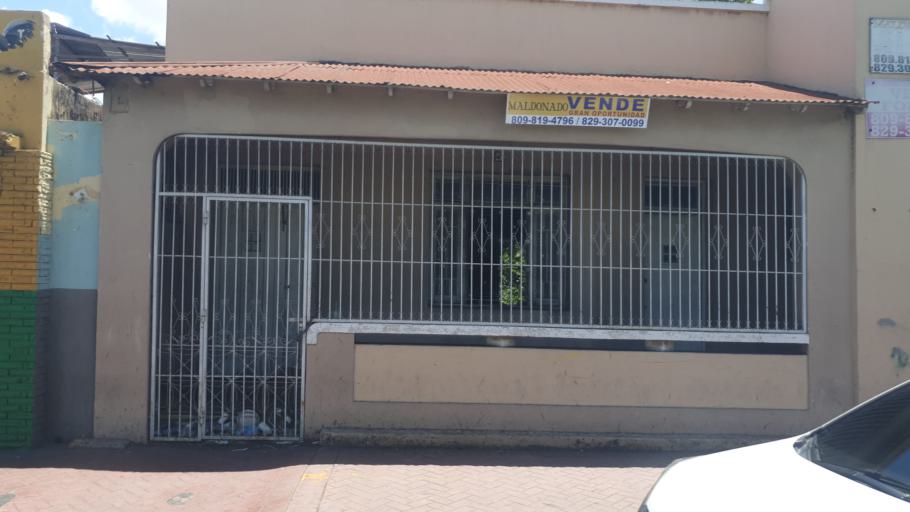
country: DO
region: Santiago
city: Santiago de los Caballeros
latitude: 19.4493
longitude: -70.7054
